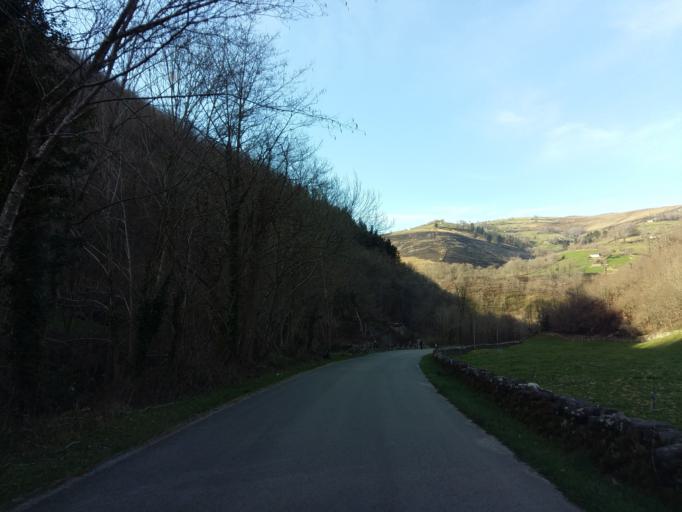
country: ES
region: Cantabria
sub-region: Provincia de Cantabria
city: Vega de Pas
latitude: 43.1533
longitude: -3.8056
